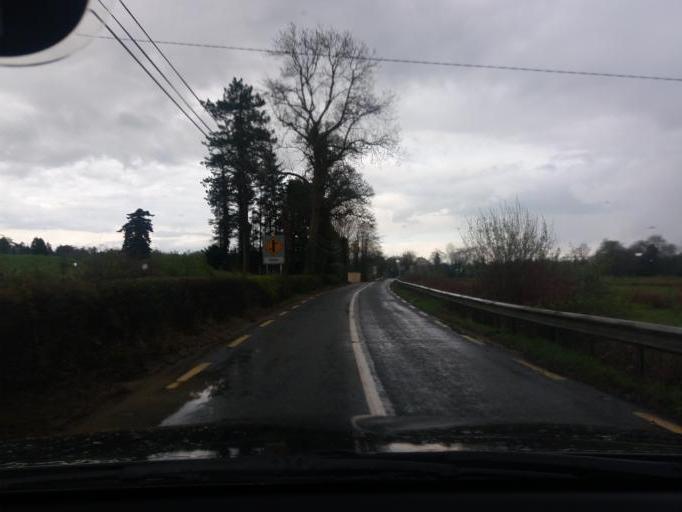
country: IE
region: Ulster
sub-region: An Cabhan
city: Ballyconnell
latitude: 54.1275
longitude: -7.6828
